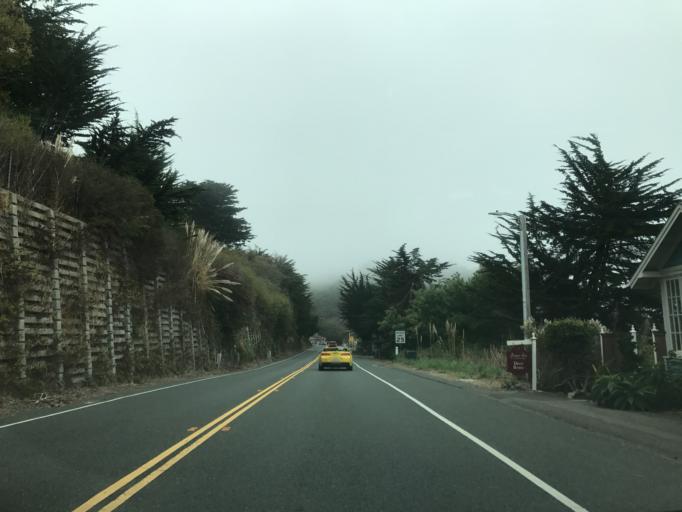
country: US
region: California
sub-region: Sonoma County
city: Monte Rio
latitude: 38.4503
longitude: -123.1181
